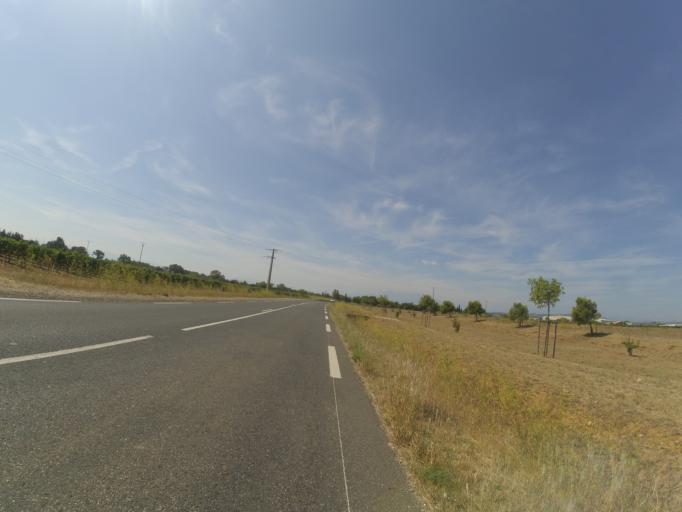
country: FR
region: Languedoc-Roussillon
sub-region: Departement des Pyrenees-Orientales
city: Rivesaltes
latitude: 42.7808
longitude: 2.8868
